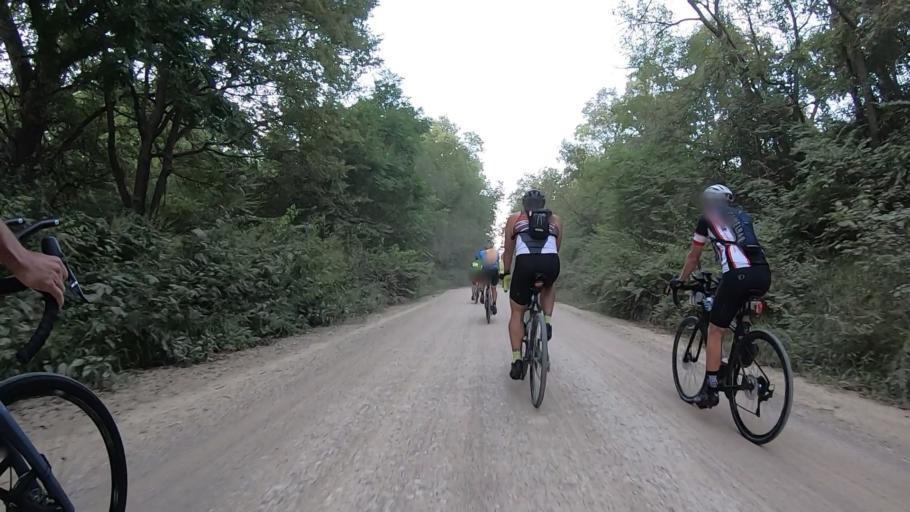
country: US
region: Kansas
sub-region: Marshall County
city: Marysville
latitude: 39.8403
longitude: -96.6645
